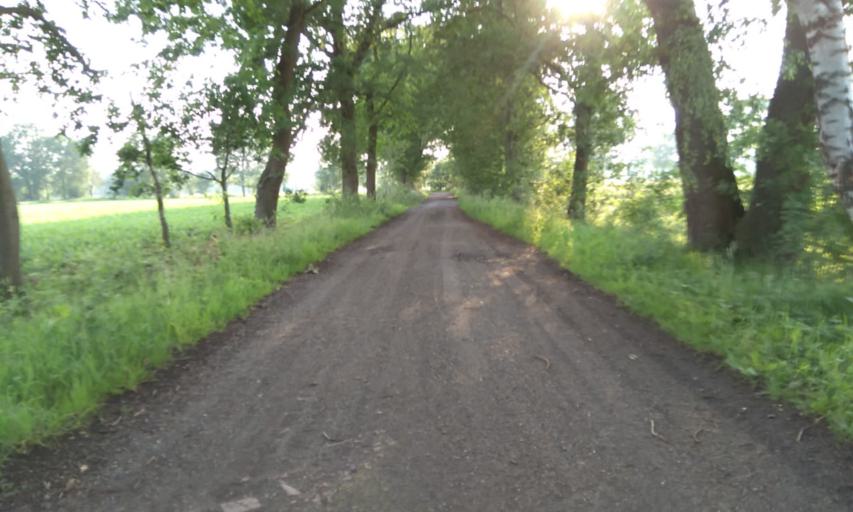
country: DE
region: Lower Saxony
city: Bliedersdorf
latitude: 53.4345
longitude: 9.5589
